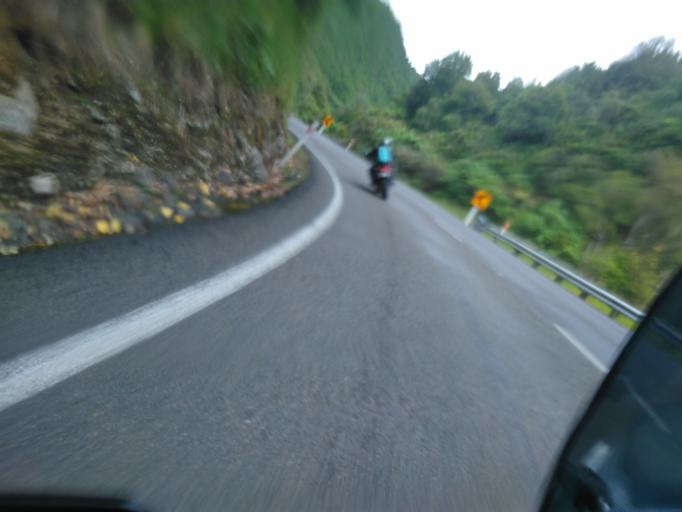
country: NZ
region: Bay of Plenty
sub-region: Opotiki District
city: Opotiki
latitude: -38.2970
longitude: 177.3913
